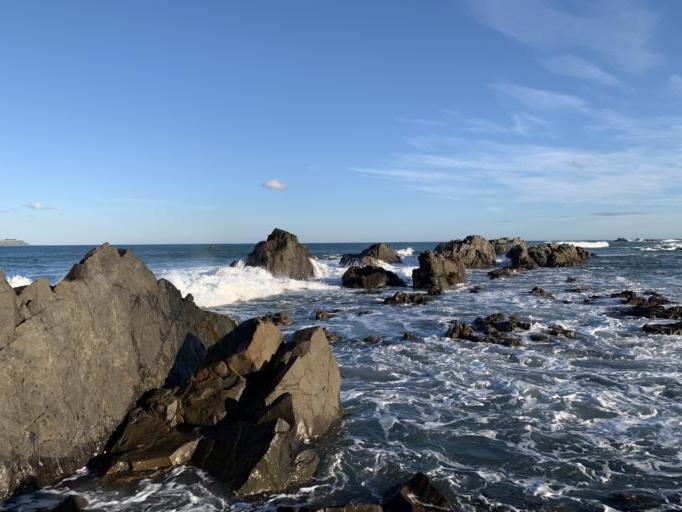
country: NZ
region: Wellington
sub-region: Wellington City
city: Wellington
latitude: -41.3445
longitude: 174.8214
